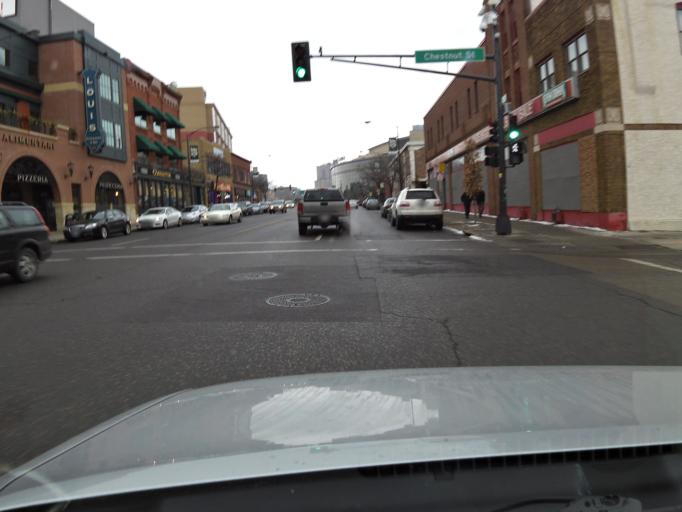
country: US
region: Minnesota
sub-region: Ramsey County
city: Saint Paul
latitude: 44.9434
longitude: -93.1041
